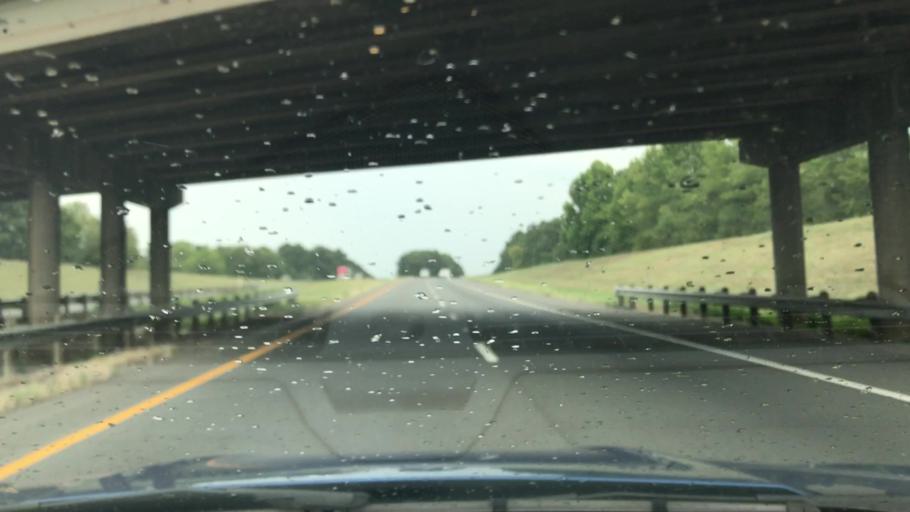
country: US
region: Texas
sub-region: Harrison County
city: Marshall
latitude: 32.4889
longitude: -94.4098
